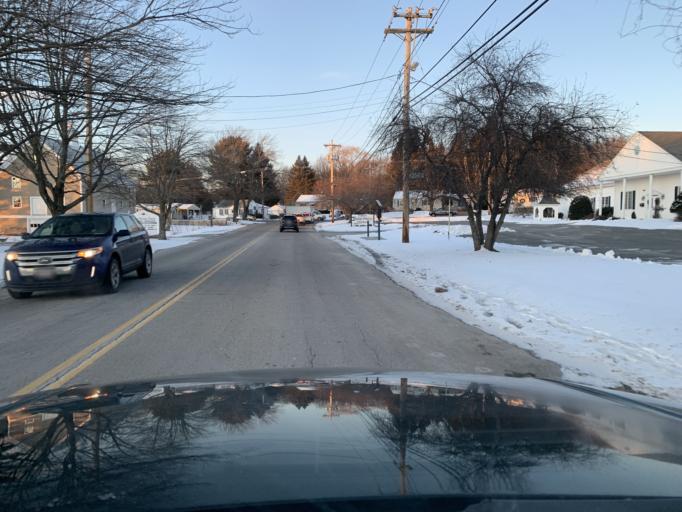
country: US
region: Massachusetts
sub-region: Essex County
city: Haverhill
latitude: 42.7813
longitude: -71.1117
